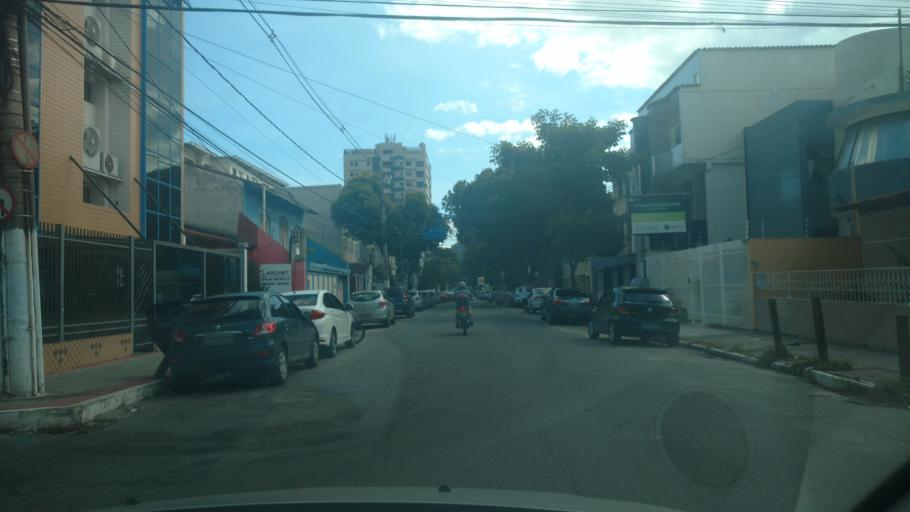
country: BR
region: Espirito Santo
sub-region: Vila Velha
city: Vila Velha
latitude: -20.3340
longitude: -40.2869
